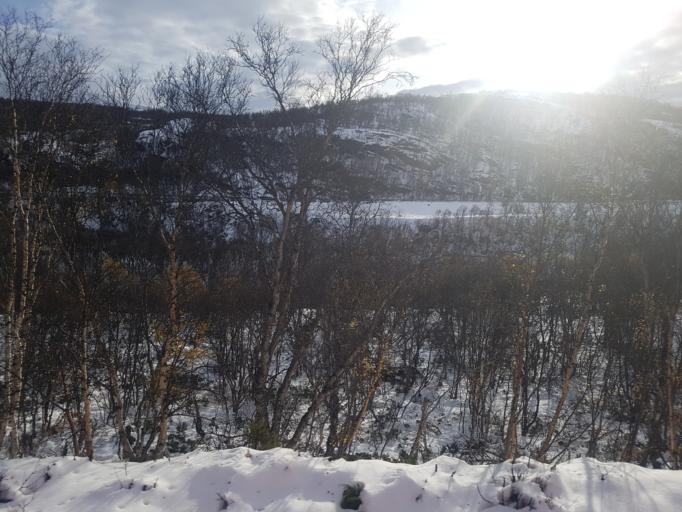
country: NO
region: Sor-Trondelag
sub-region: Oppdal
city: Oppdal
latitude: 62.2991
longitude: 9.6015
